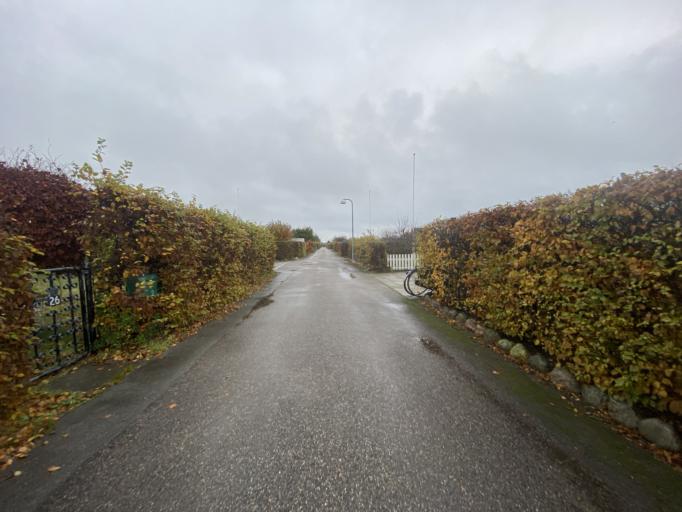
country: DK
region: Capital Region
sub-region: Dragor Kommune
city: Dragor
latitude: 55.5793
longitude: 12.6326
